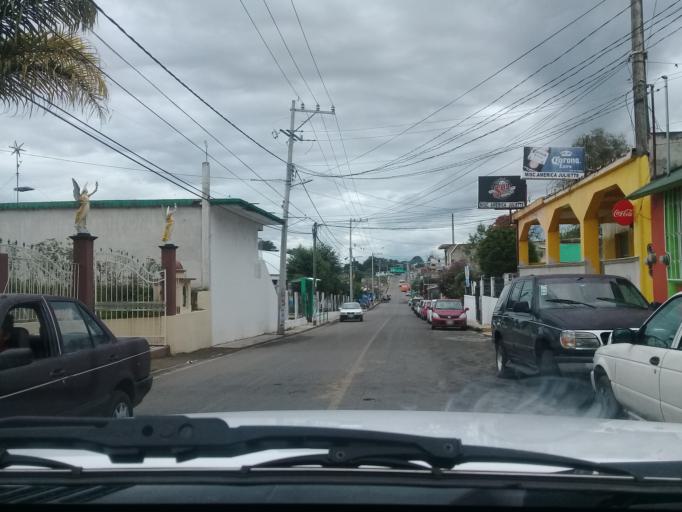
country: MX
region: Veracruz
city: Rafael Lucio
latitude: 19.5984
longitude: -96.9893
